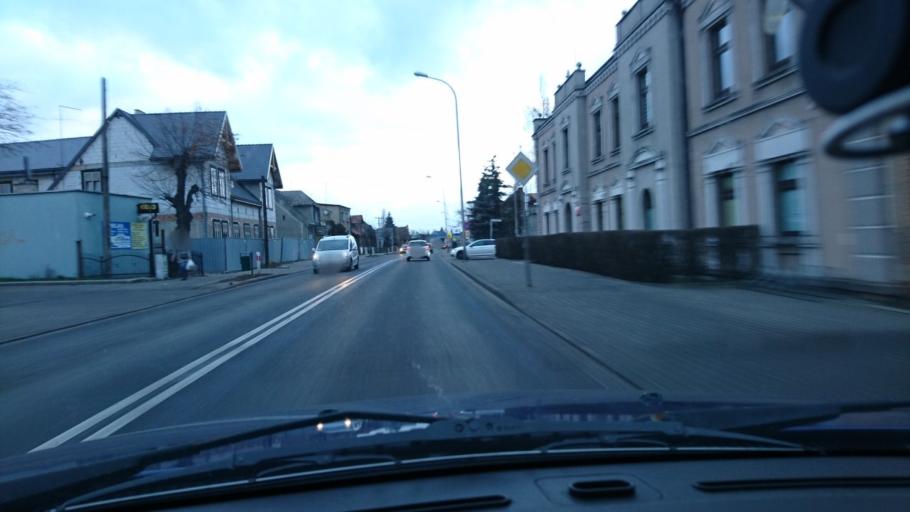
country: PL
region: Greater Poland Voivodeship
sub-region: Powiat kepinski
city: Kepno
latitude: 51.2858
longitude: 17.9930
